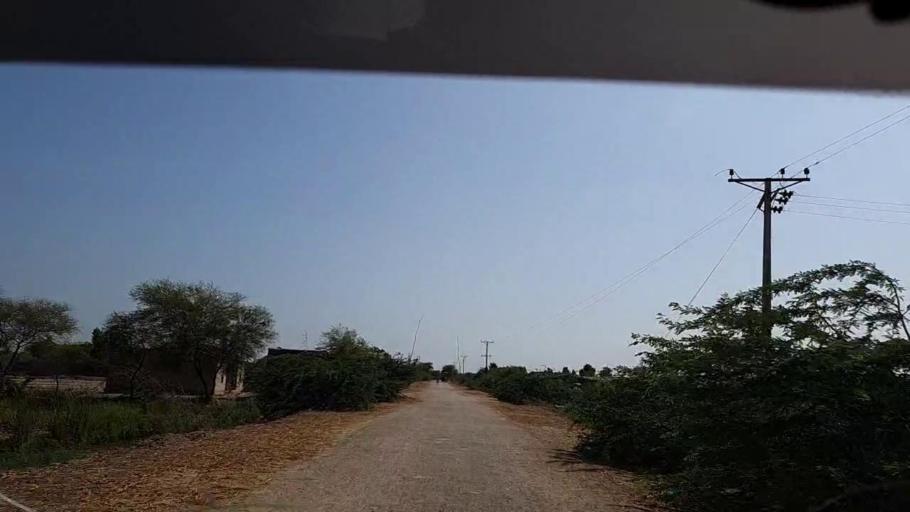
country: PK
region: Sindh
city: Badin
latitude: 24.6387
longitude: 68.7871
